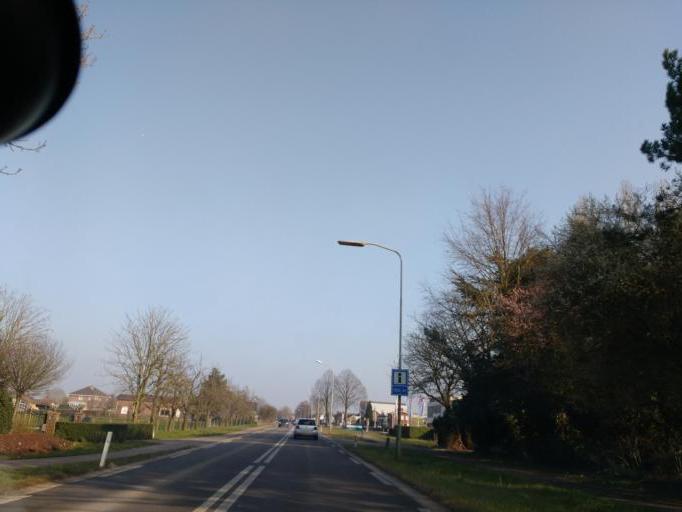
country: NL
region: Gelderland
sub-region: Gemeente Groesbeek
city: Berg en Dal
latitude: 51.8794
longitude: 5.9399
